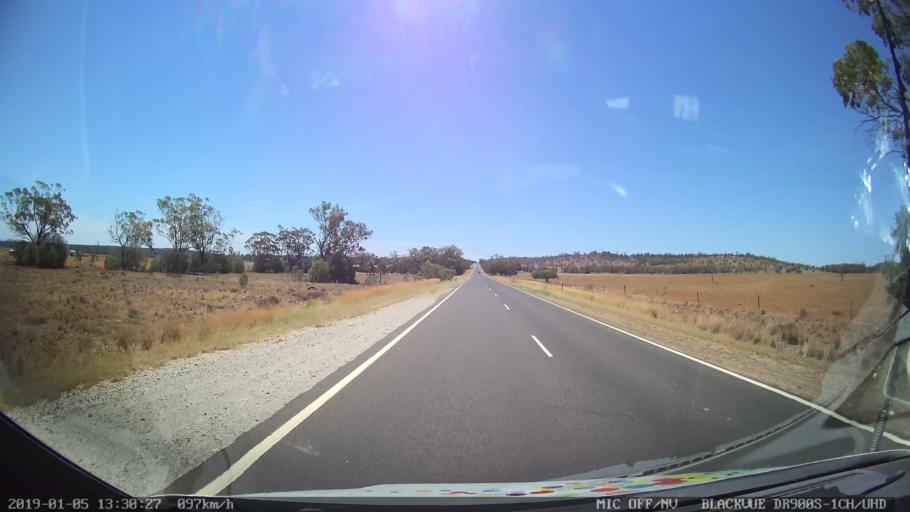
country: AU
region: New South Wales
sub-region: Gunnedah
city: Gunnedah
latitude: -31.0189
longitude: 150.0707
